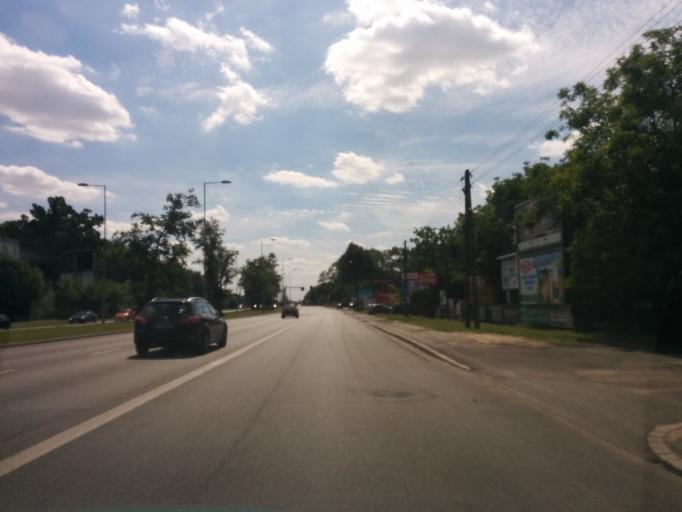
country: PL
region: Masovian Voivodeship
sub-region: Warszawa
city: Bialoleka
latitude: 52.3257
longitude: 20.9687
